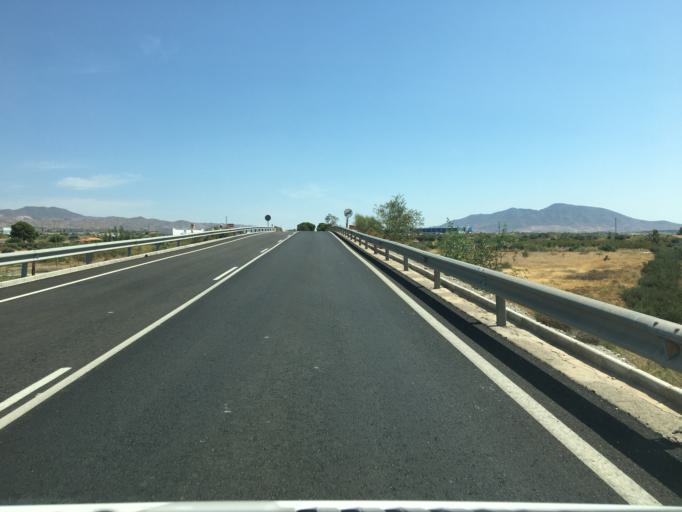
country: ES
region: Andalusia
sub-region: Provincia de Almeria
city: Huercal-Overa
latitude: 37.4268
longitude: -1.9159
